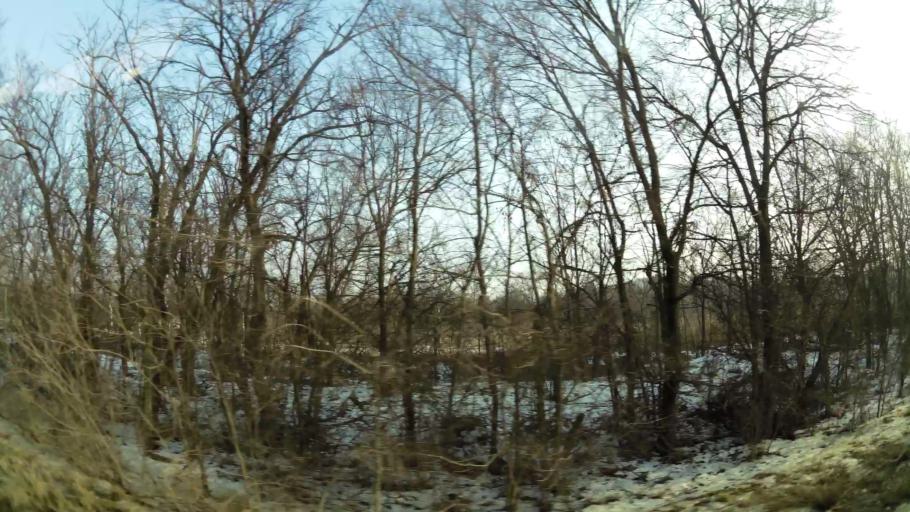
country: MK
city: Kadino
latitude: 41.9778
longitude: 21.6121
